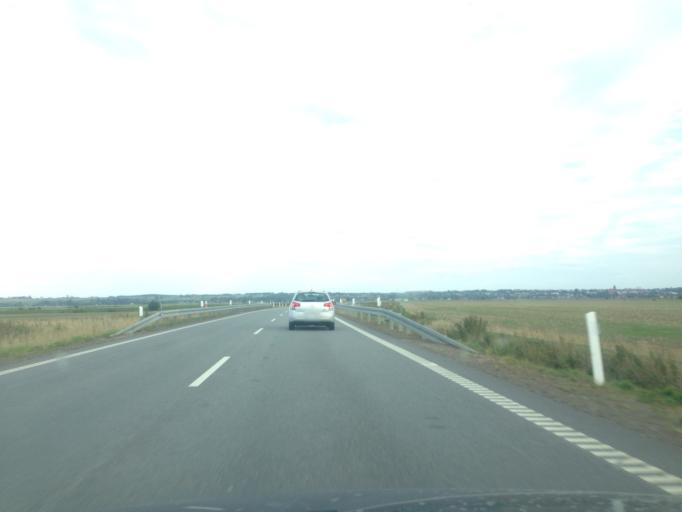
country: PL
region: Pomeranian Voivodeship
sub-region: Powiat kwidzynski
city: Kwidzyn
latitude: 53.7610
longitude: 18.8712
